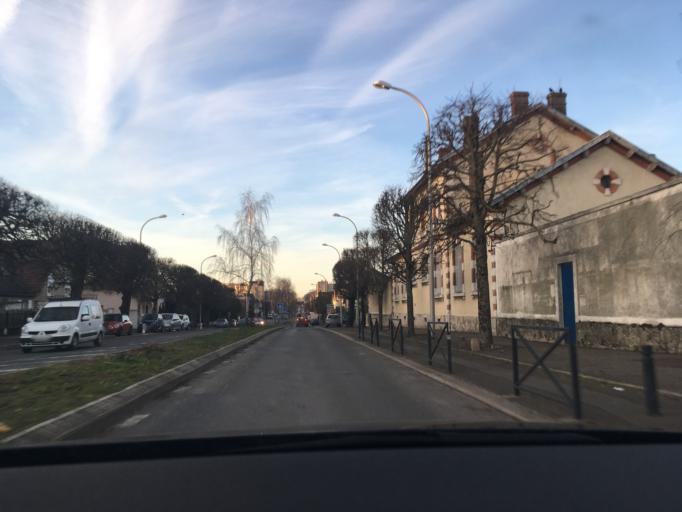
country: FR
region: Ile-de-France
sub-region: Departement de Seine-et-Marne
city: Melun
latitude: 48.5464
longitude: 2.6519
